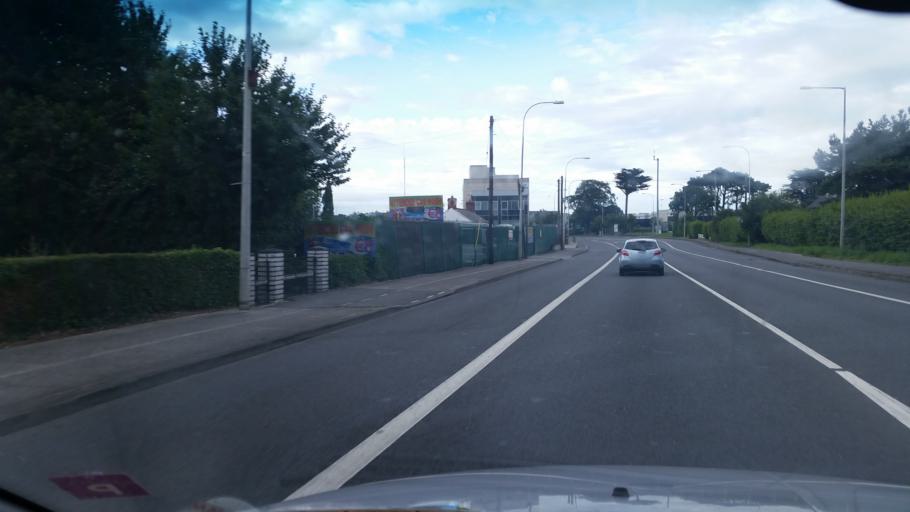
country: IE
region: Leinster
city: Beaumont
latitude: 53.4059
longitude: -6.2387
